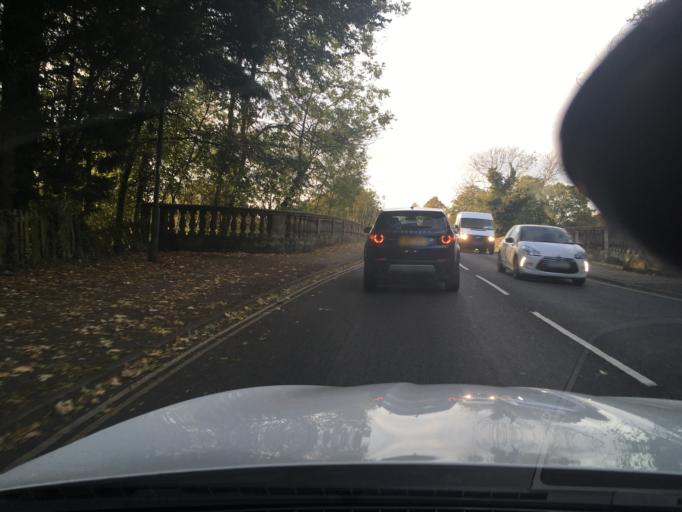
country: GB
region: England
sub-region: Warwickshire
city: Warwick
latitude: 52.2791
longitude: -1.5791
